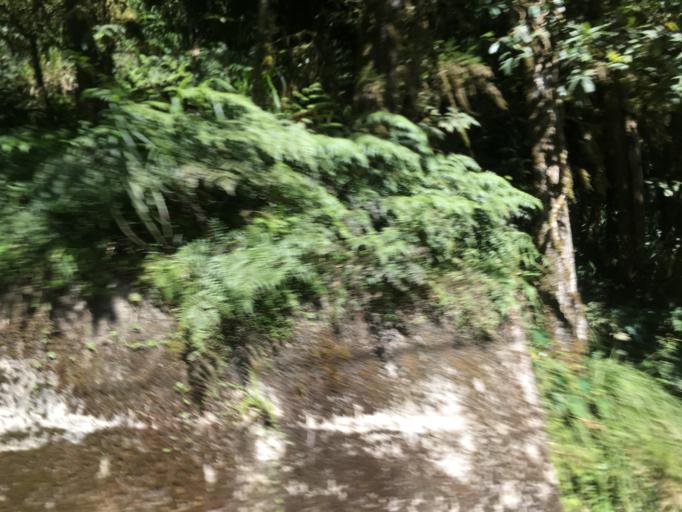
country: TW
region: Taiwan
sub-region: Yilan
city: Yilan
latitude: 24.6222
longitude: 121.4783
